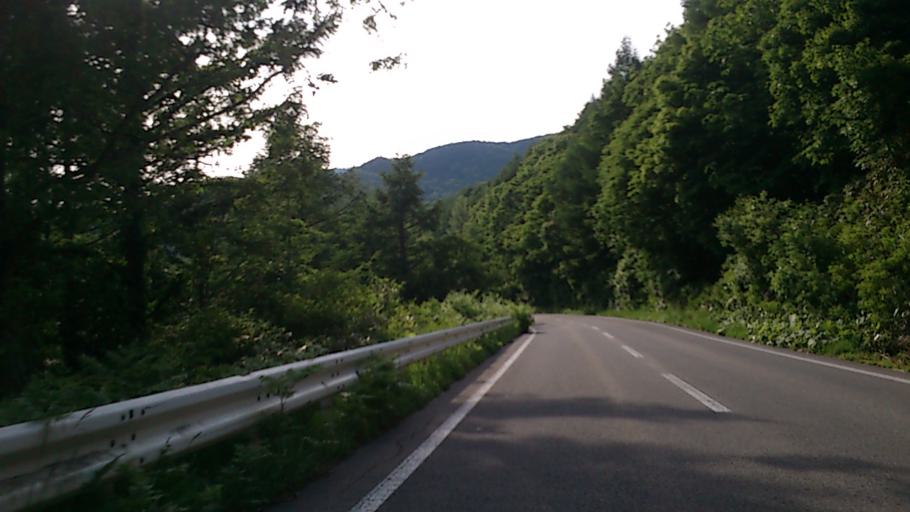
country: JP
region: Aomori
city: Aomori Shi
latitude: 40.6504
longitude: 140.7739
